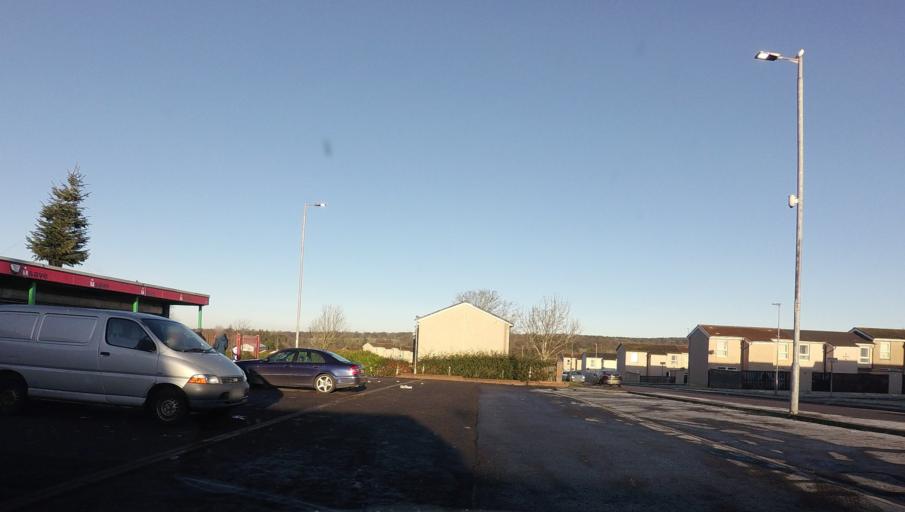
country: GB
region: Scotland
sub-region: North Lanarkshire
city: Newmains
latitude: 55.7896
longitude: -3.8853
